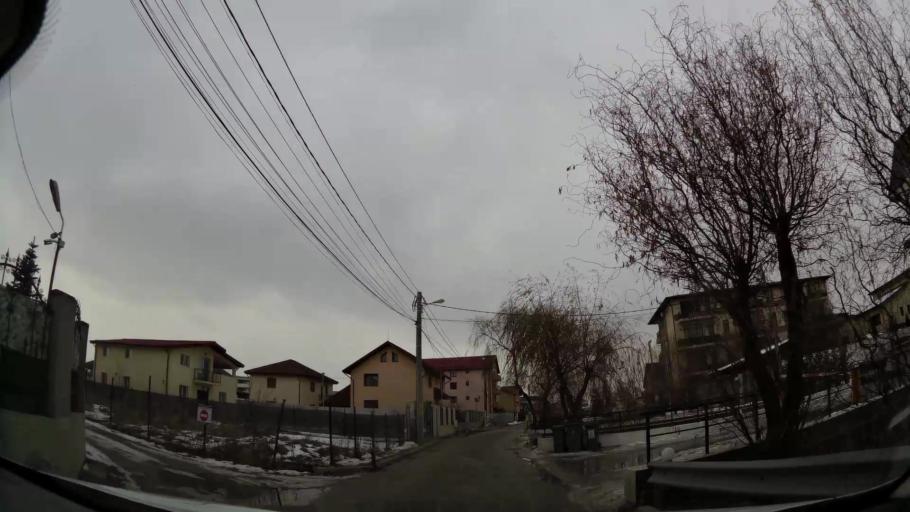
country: RO
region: Ilfov
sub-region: Comuna Otopeni
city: Otopeni
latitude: 44.5430
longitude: 26.0744
